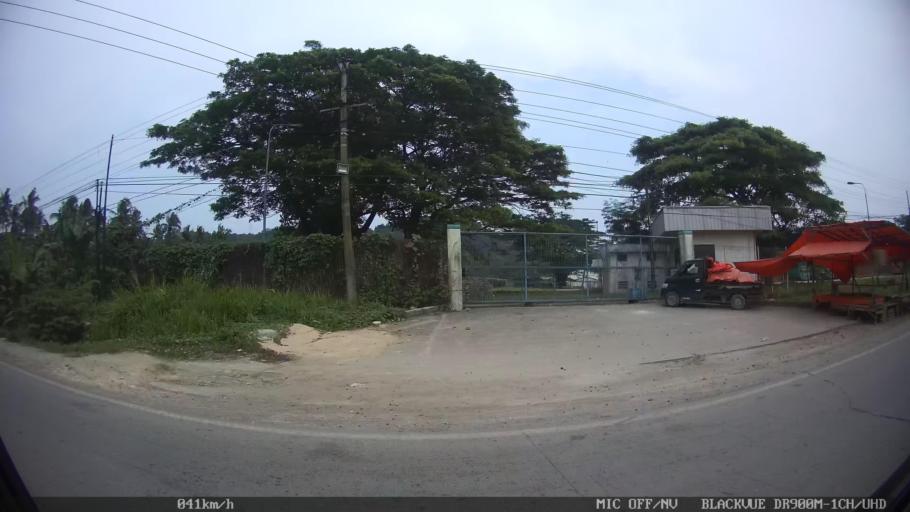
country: ID
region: Lampung
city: Panjang
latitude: -5.4192
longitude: 105.3396
